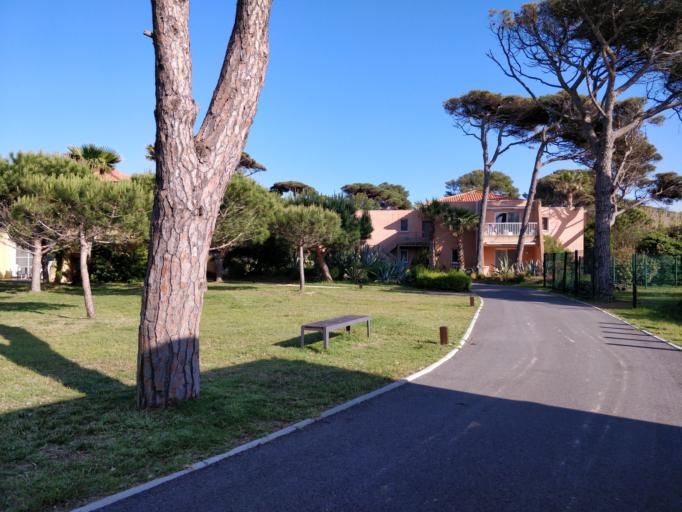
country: FR
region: Provence-Alpes-Cote d'Azur
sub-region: Departement du Var
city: Hyeres
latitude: 43.0433
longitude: 6.1477
